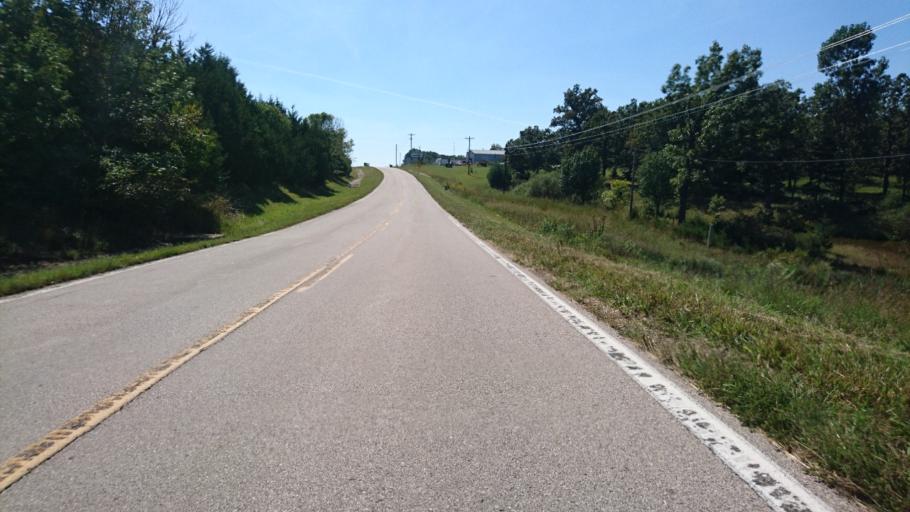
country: US
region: Missouri
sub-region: Franklin County
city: Sullivan
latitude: 38.2410
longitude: -91.1423
